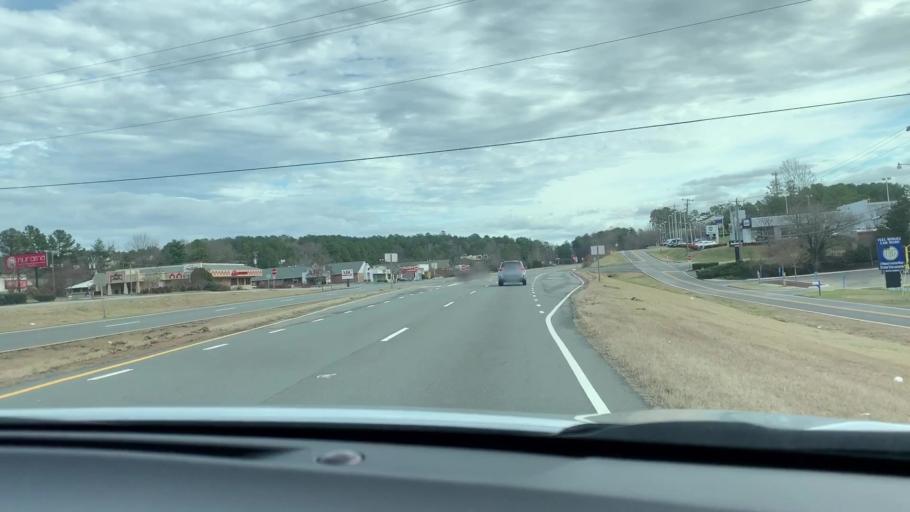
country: US
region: North Carolina
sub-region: Durham County
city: Durham
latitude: 35.9710
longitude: -78.9519
